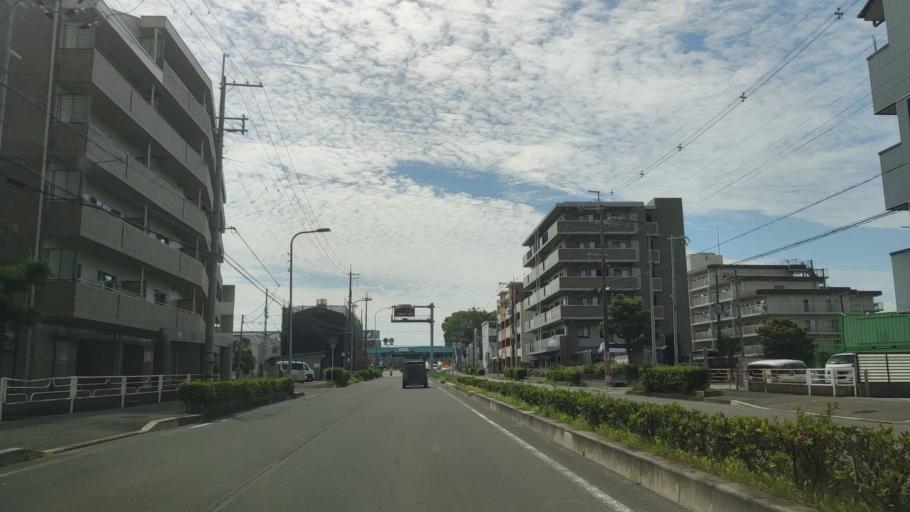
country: JP
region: Osaka
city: Ikeda
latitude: 34.8039
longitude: 135.4405
